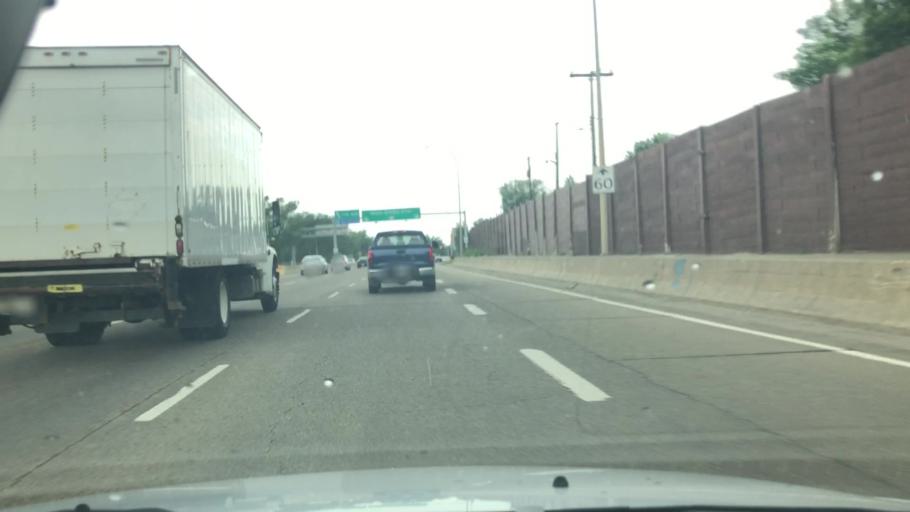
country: CA
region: Alberta
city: Edmonton
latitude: 53.5654
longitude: -113.4491
